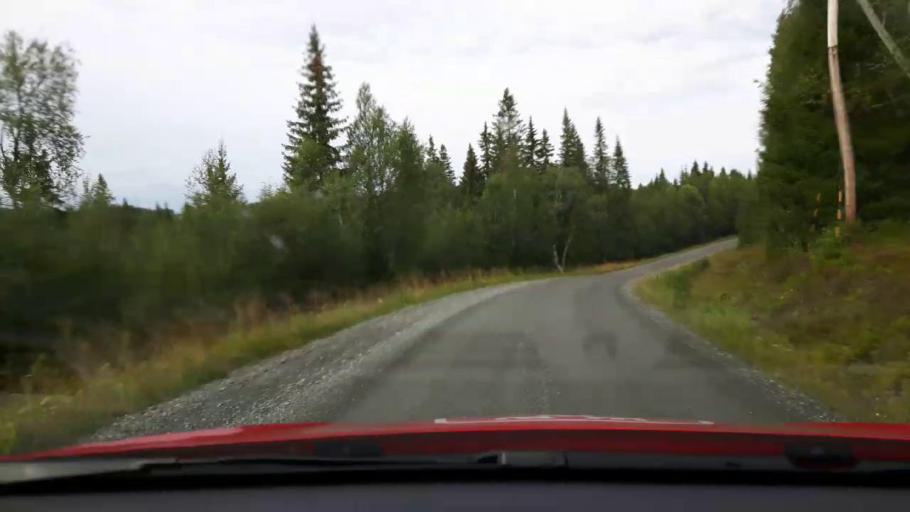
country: SE
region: Jaemtland
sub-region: Are Kommun
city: Are
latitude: 63.7688
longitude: 13.0922
